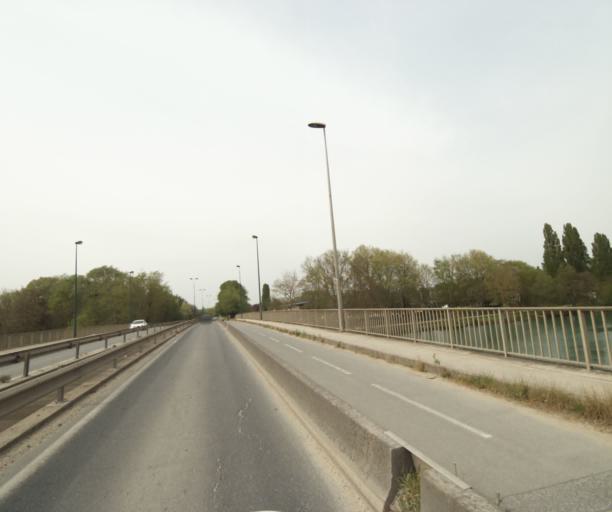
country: FR
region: Ile-de-France
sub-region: Departement de Seine-et-Marne
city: Torcy
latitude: 48.8620
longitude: 2.6446
